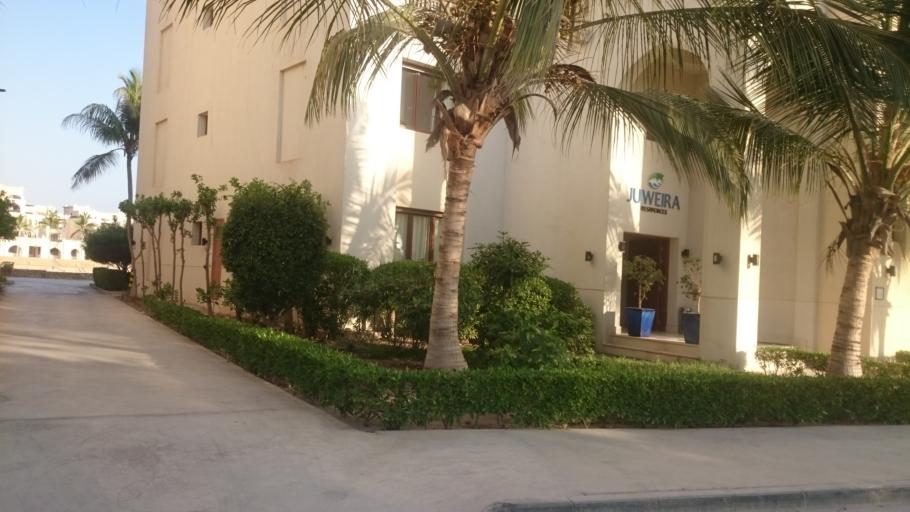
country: OM
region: Zufar
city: Salalah
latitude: 17.0322
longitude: 54.3001
